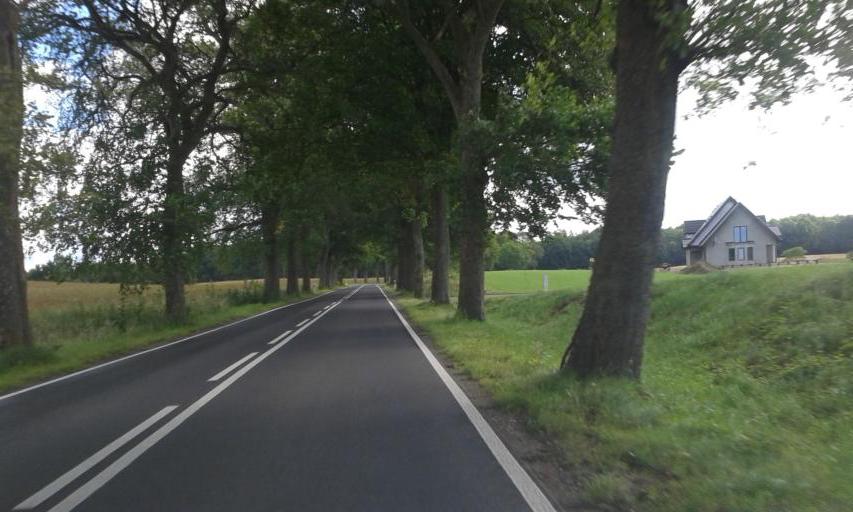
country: PL
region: West Pomeranian Voivodeship
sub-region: Powiat koszalinski
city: Bobolice
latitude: 53.9663
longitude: 16.6311
